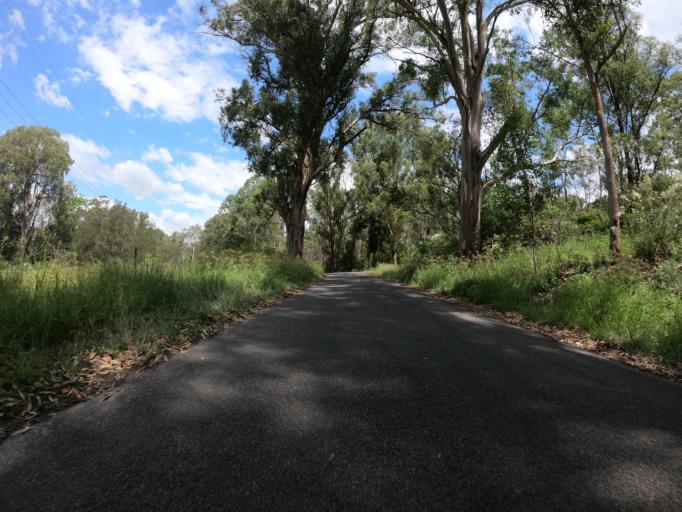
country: AU
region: New South Wales
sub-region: Penrith Municipality
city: Mulgoa
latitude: -33.8295
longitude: 150.6568
